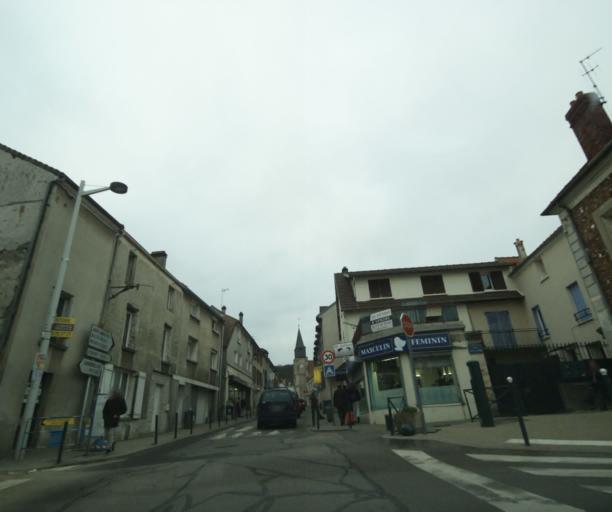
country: FR
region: Ile-de-France
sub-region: Departement des Yvelines
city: Chanteloup-les-Vignes
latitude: 48.9776
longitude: 2.0310
